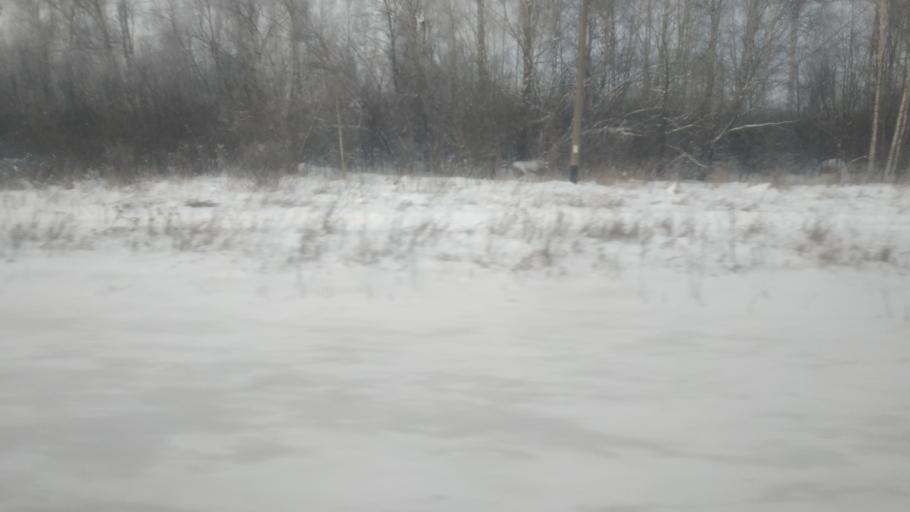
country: RU
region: Udmurtiya
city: Kizner
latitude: 56.3904
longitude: 51.7264
